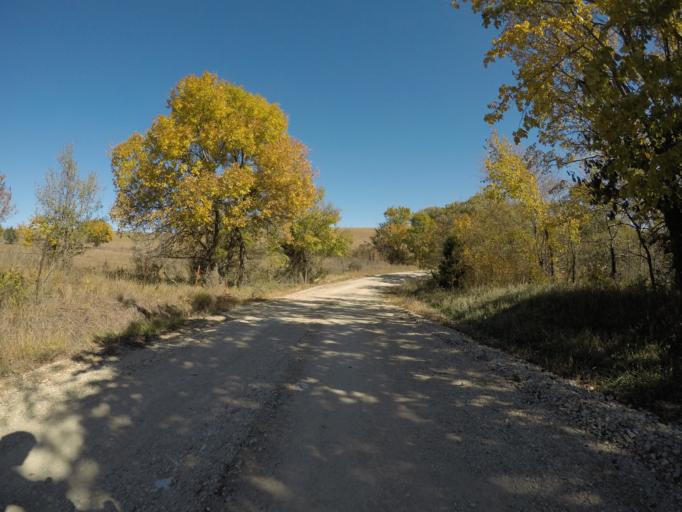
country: US
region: Kansas
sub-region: Wabaunsee County
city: Alma
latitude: 38.9835
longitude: -96.4560
